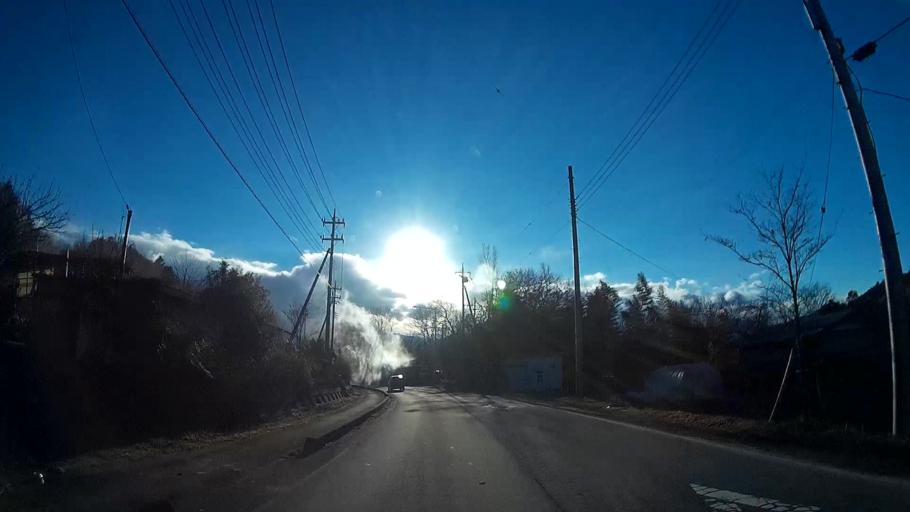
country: JP
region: Saitama
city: Chichibu
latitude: 36.0478
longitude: 139.0506
